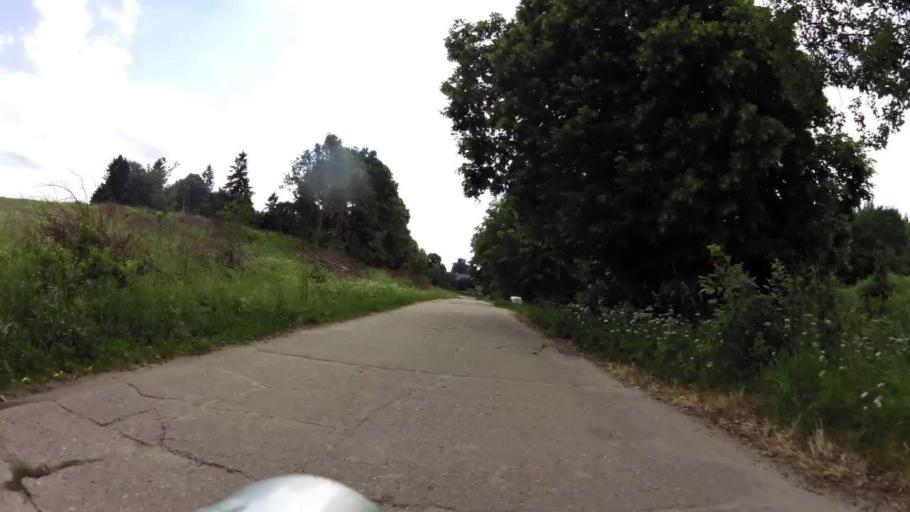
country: PL
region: West Pomeranian Voivodeship
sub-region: Powiat koszalinski
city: Bobolice
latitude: 53.9619
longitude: 16.6921
